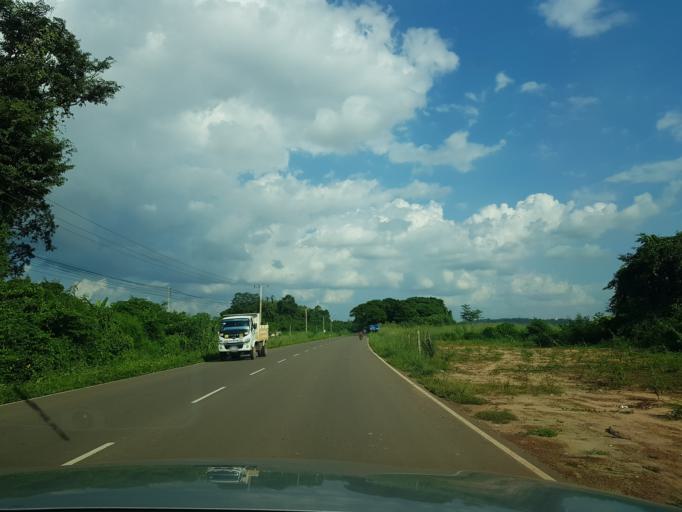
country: TH
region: Nong Khai
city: Si Chiang Mai
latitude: 17.9758
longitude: 102.4753
